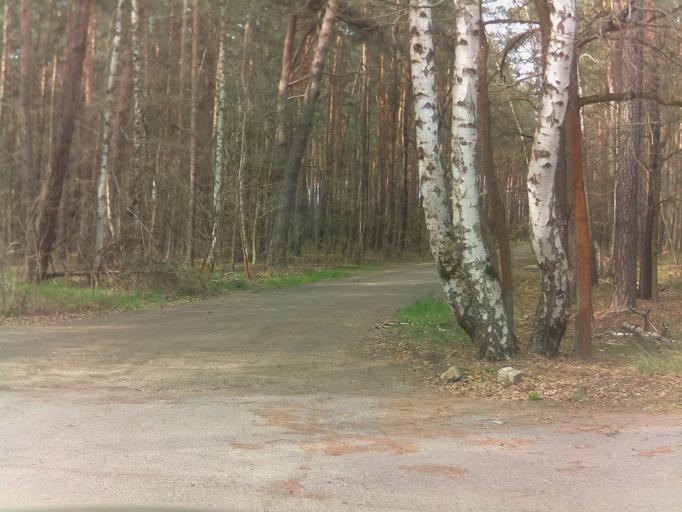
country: DE
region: Brandenburg
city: Cottbus
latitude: 51.7979
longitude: 14.3381
